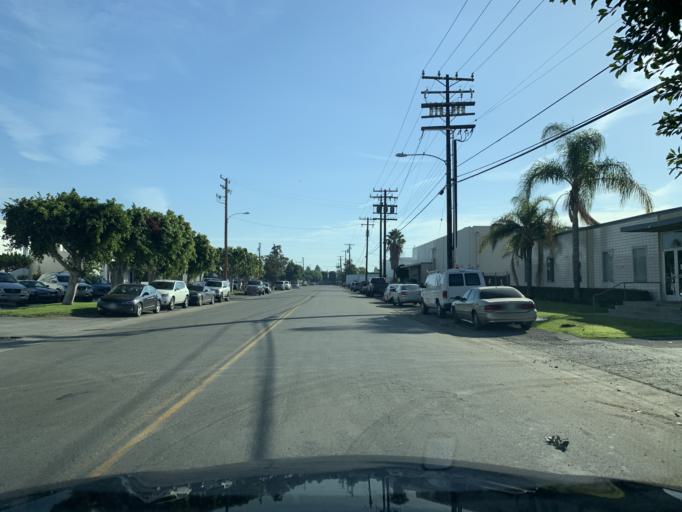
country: US
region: California
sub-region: Orange County
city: Anaheim
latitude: 33.8171
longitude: -117.9052
